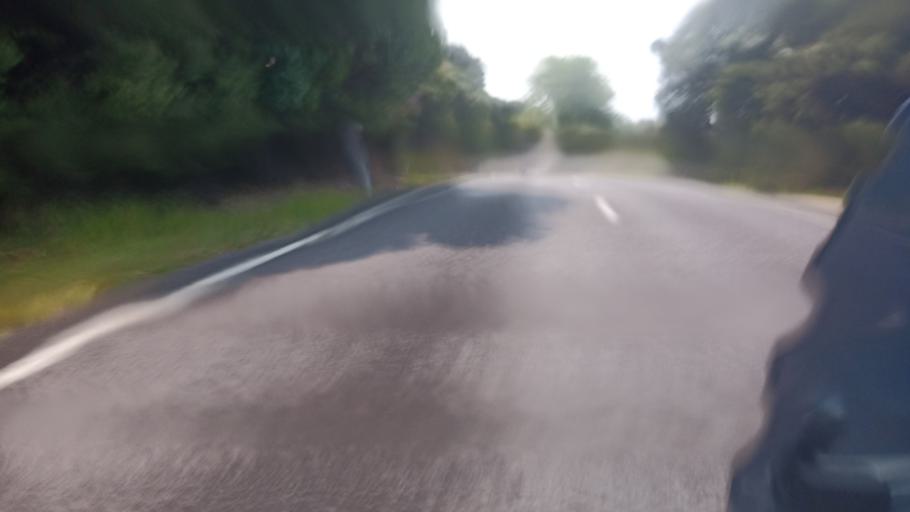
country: NZ
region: Bay of Plenty
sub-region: Opotiki District
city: Opotiki
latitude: -37.6622
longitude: 177.8255
